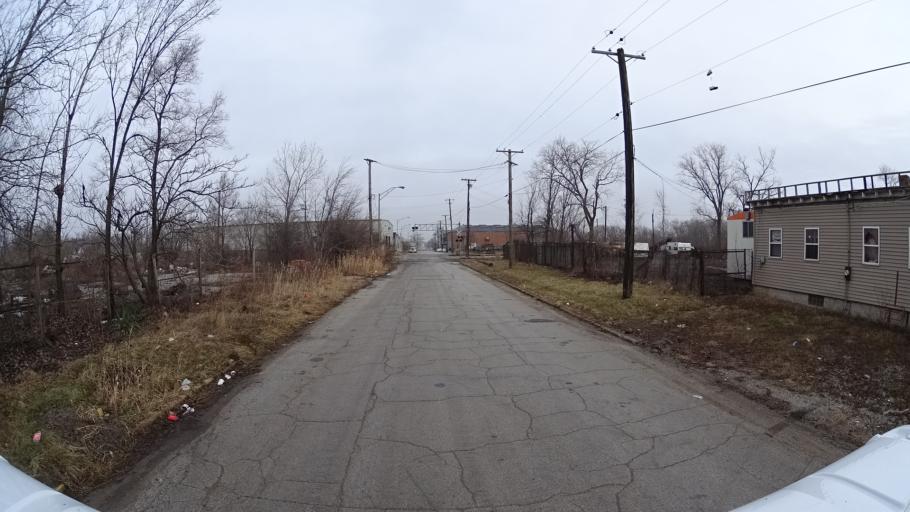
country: US
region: Illinois
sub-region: Cook County
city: Chicago Heights
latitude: 41.5000
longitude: -87.6210
